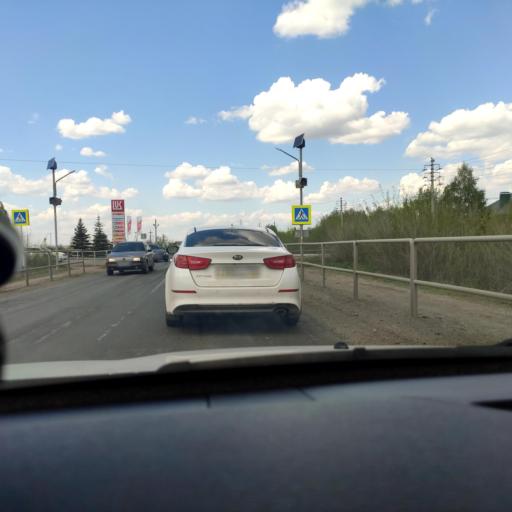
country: RU
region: Samara
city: Kinel'
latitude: 53.2138
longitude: 50.6149
